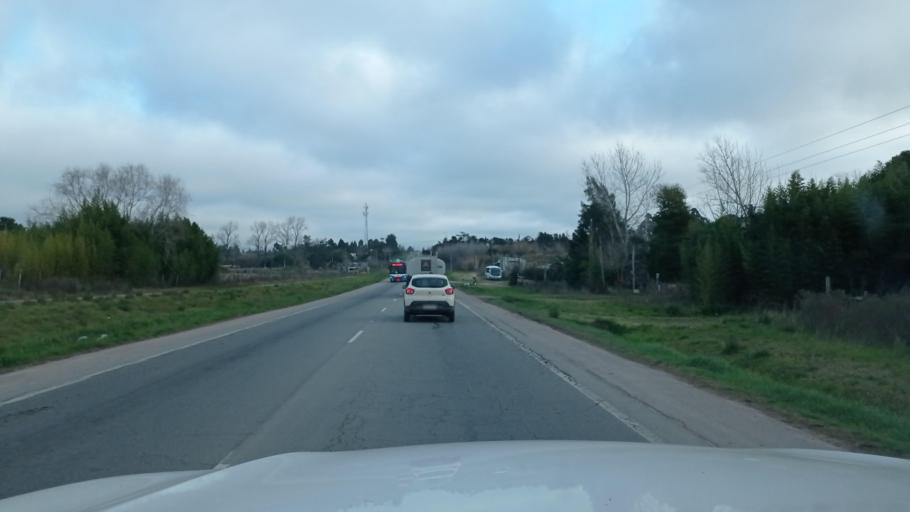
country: UY
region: Canelones
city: Toledo
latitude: -34.7652
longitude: -56.1202
